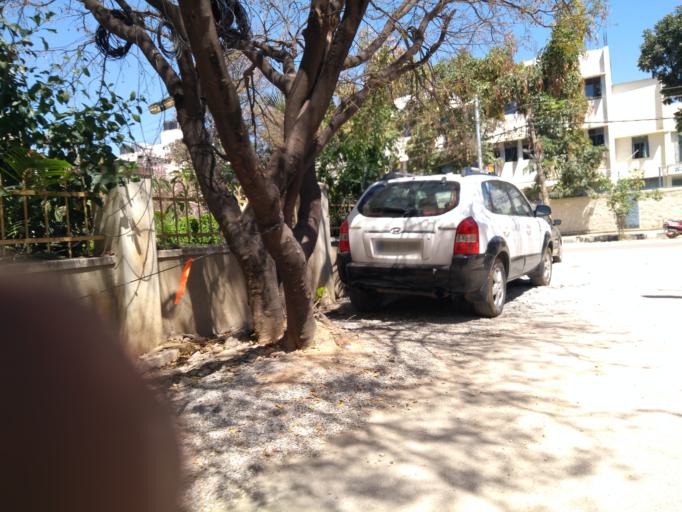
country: IN
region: Karnataka
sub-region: Bangalore Urban
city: Bangalore
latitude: 12.9682
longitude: 77.6545
